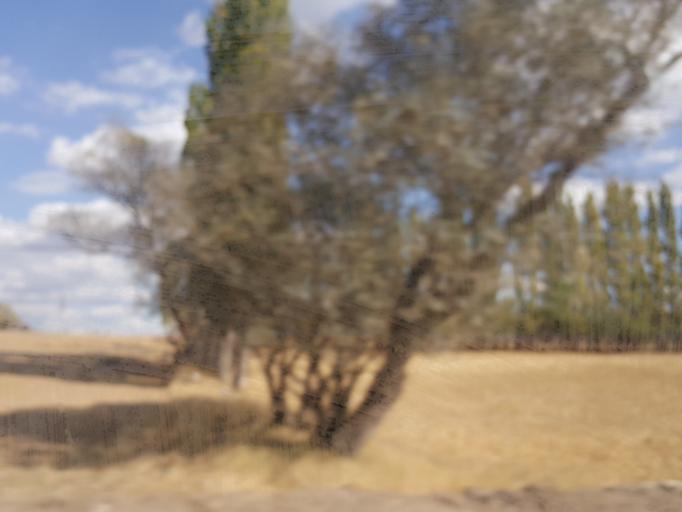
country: TR
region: Tokat
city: Artova
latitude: 40.0501
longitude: 36.3012
